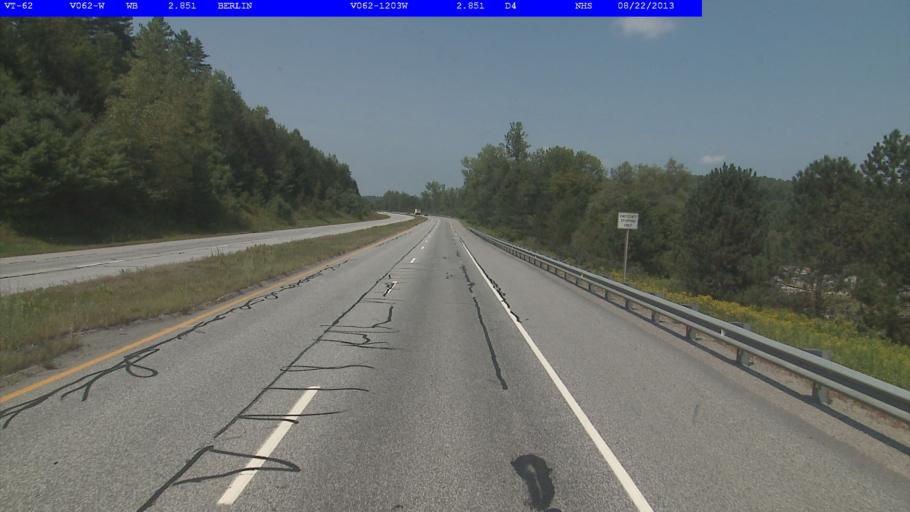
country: US
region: Vermont
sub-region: Washington County
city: Barre
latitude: 44.2101
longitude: -72.5224
